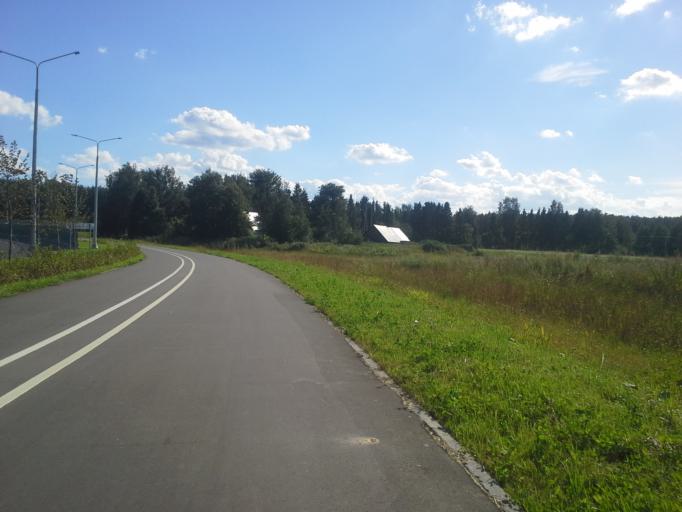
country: RU
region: Moskovskaya
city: Kokoshkino
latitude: 55.5681
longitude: 37.1532
